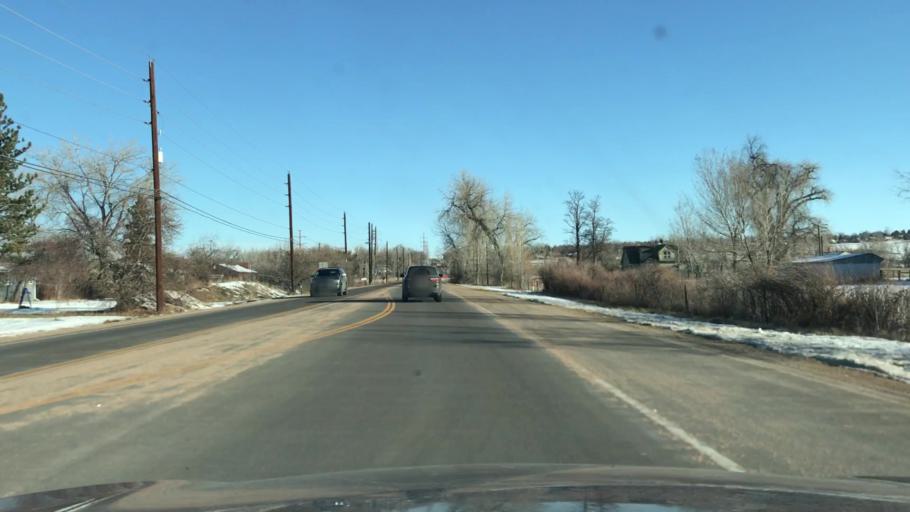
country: US
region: Colorado
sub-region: Boulder County
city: Gunbarrel
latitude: 40.0456
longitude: -105.1783
